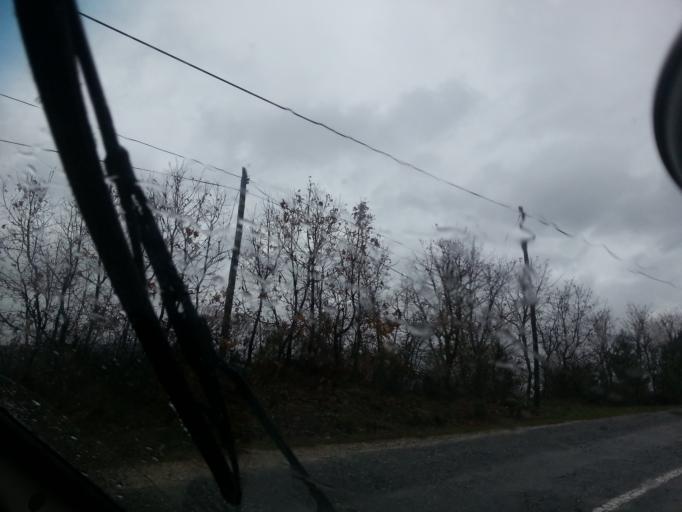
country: PT
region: Guarda
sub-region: Fornos de Algodres
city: Fornos de Algodres
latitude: 40.6260
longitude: -7.4721
